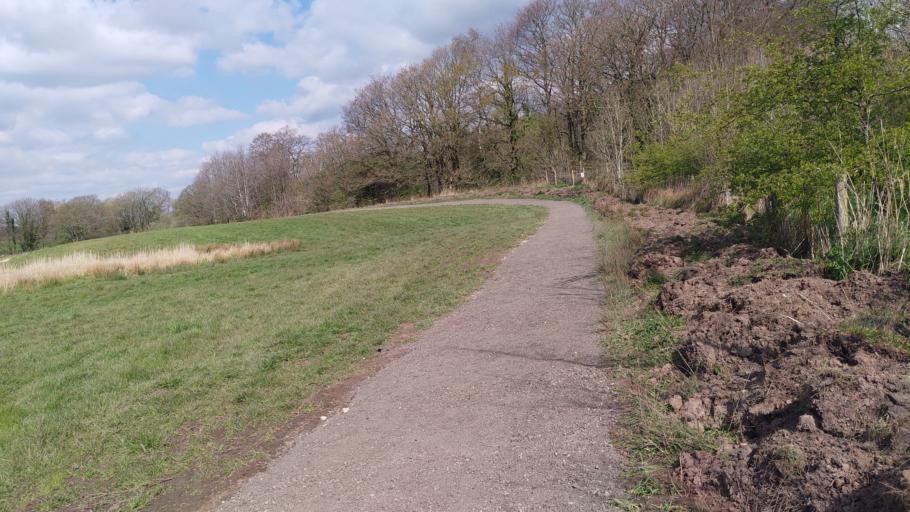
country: GB
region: England
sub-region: Lancashire
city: Coppull
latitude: 53.6463
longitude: -2.6554
